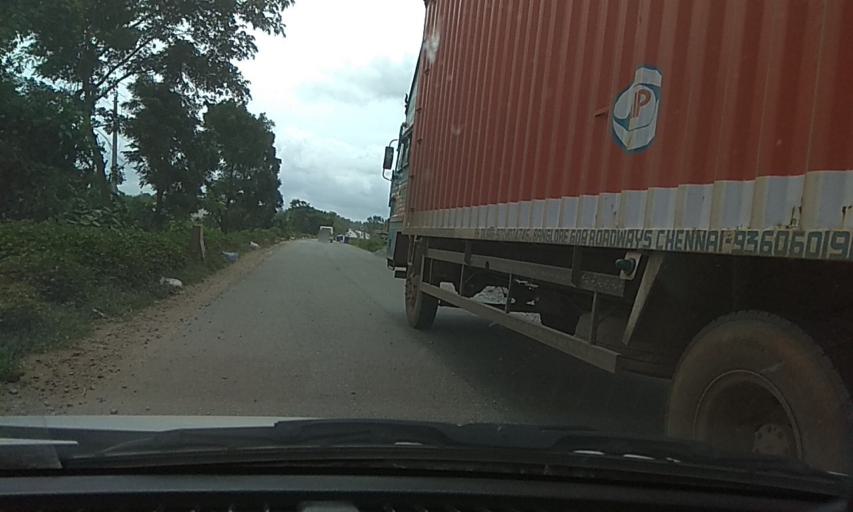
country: IN
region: Karnataka
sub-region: Davanagere
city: Mayakonda
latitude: 14.3900
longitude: 76.0586
